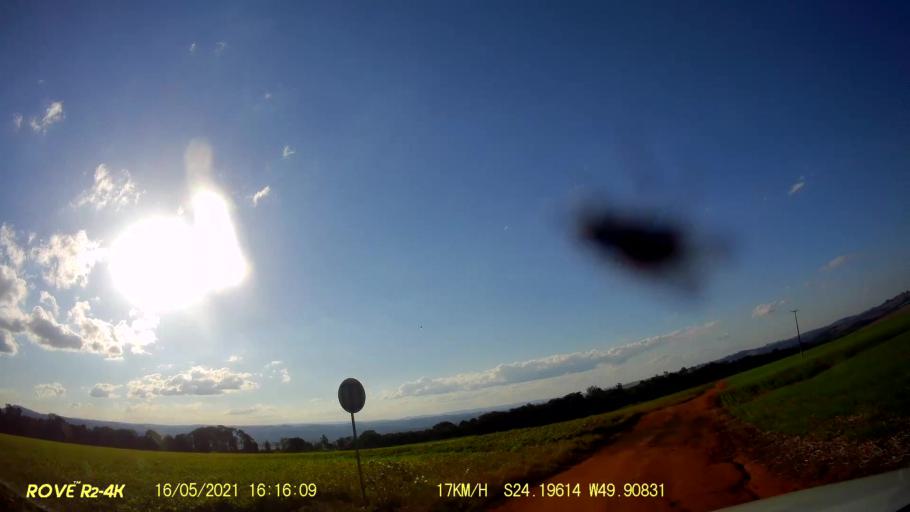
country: BR
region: Parana
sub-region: Jaguariaiva
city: Jaguariaiva
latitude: -24.1949
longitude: -49.9074
